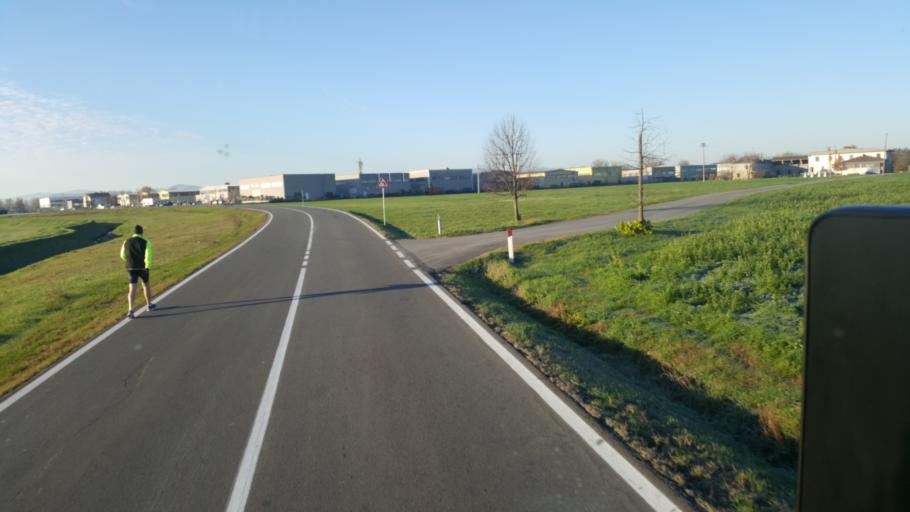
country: IT
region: Emilia-Romagna
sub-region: Provincia di Parma
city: Fontevivo
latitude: 44.8656
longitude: 10.1749
